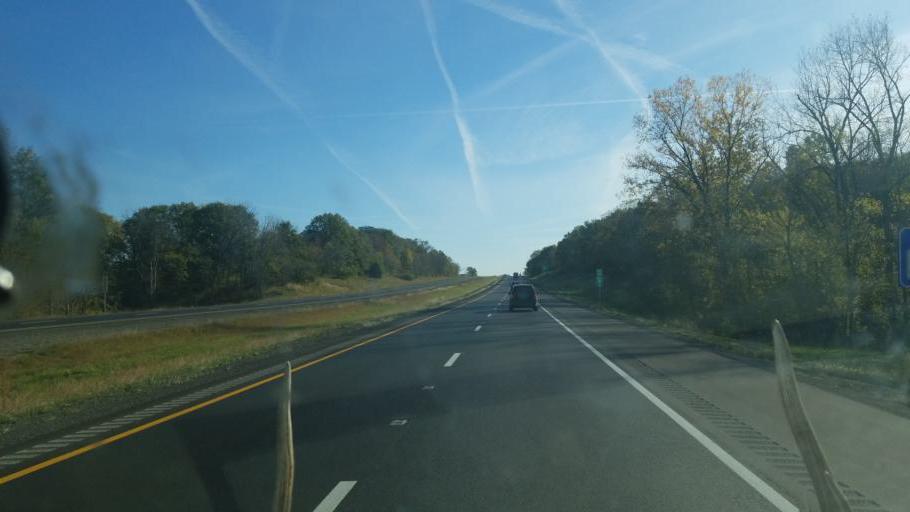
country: US
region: Illinois
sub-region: Madison County
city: Highland
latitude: 38.7863
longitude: -89.6580
